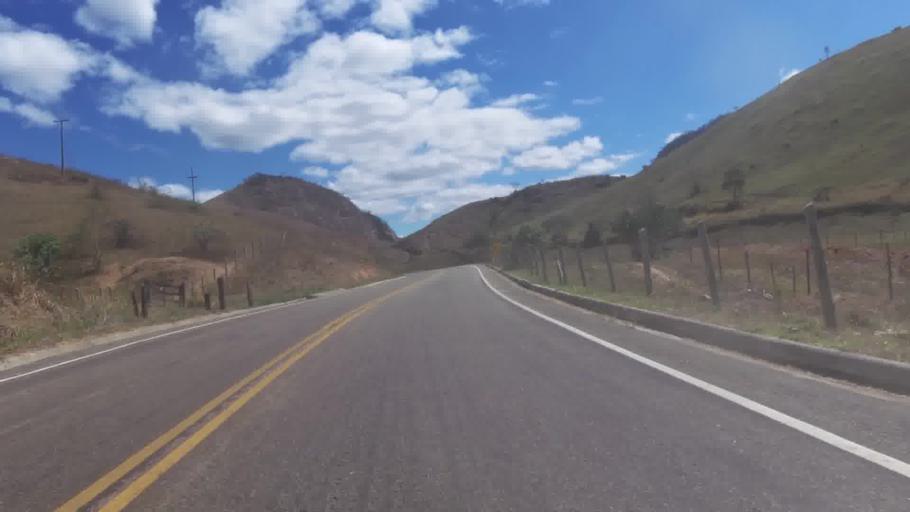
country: BR
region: Espirito Santo
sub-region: Cachoeiro De Itapemirim
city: Cachoeiro de Itapemirim
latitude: -20.9081
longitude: -41.2438
